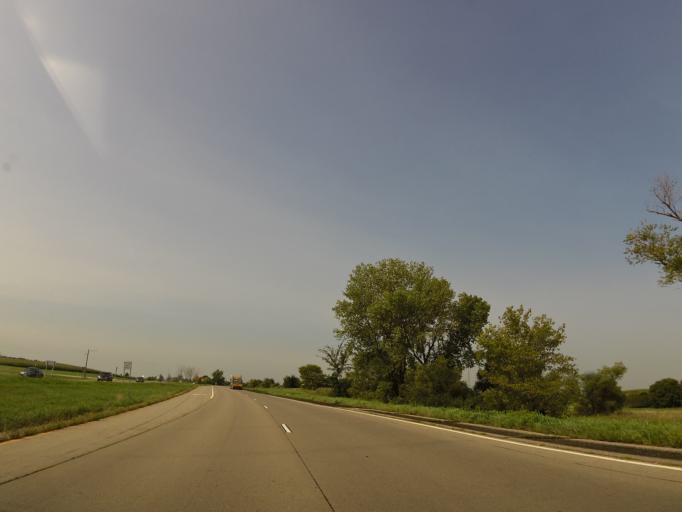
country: US
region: Minnesota
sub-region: Carver County
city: Cologne
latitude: 44.7693
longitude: -93.7971
